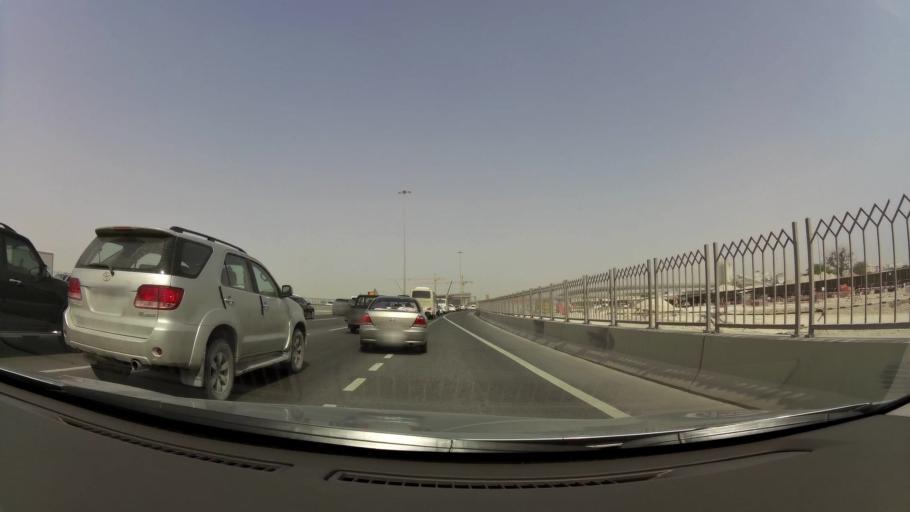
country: QA
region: Baladiyat ad Dawhah
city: Doha
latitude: 25.2906
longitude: 51.4776
